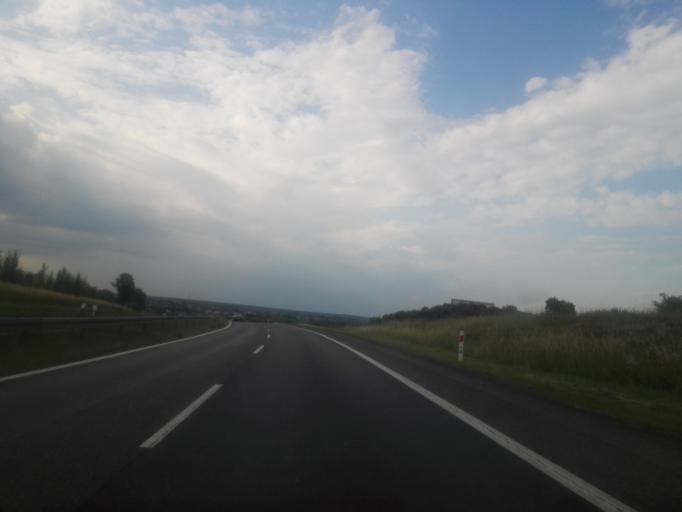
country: PL
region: Silesian Voivodeship
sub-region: Powiat myszkowski
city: Kozieglowy
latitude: 50.5825
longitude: 19.1642
